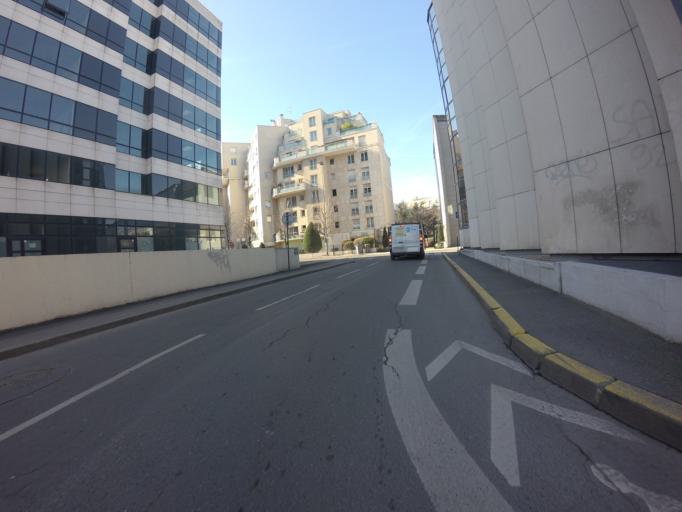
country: FR
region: Ile-de-France
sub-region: Departement des Hauts-de-Seine
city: Clichy
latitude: 48.9048
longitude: 2.3190
